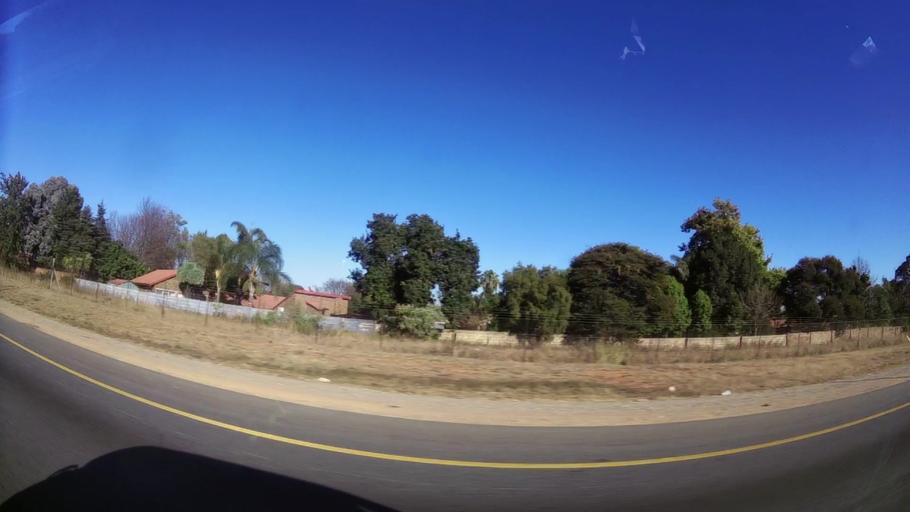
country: ZA
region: Gauteng
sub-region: City of Tshwane Metropolitan Municipality
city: Centurion
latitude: -25.8413
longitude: 28.2489
